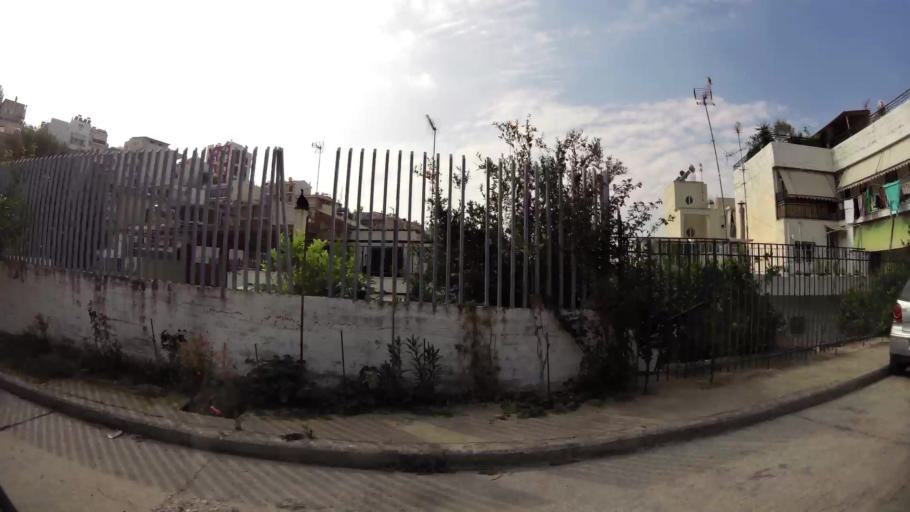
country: GR
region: Attica
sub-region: Nomarchia Athinas
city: Ilioupoli
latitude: 37.9469
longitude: 23.7642
